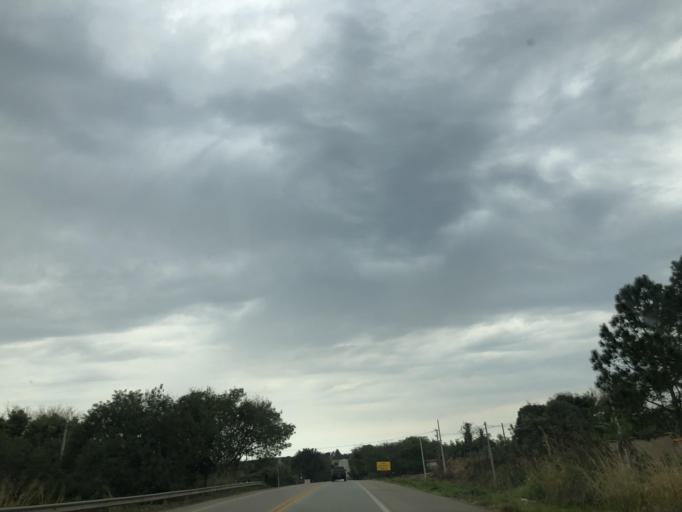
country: BR
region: Sao Paulo
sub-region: Salto De Pirapora
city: Salto de Pirapora
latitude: -23.7087
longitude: -47.6347
